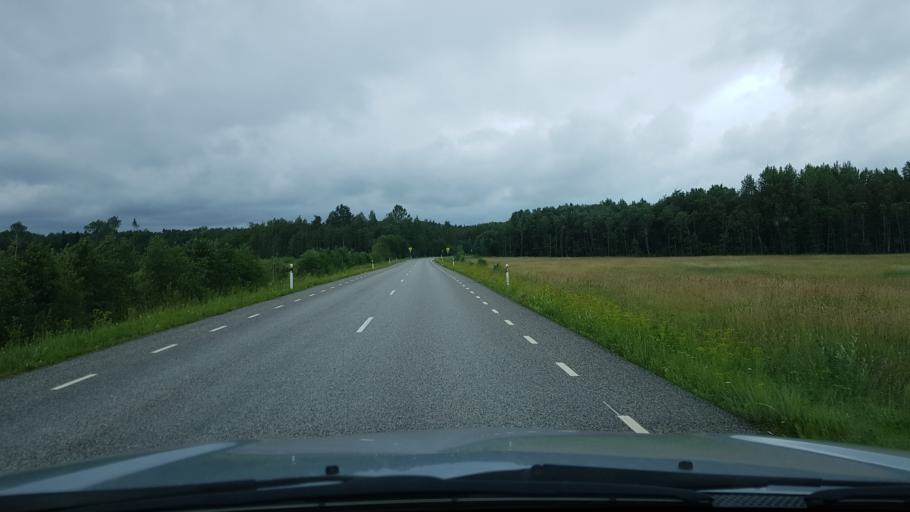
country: EE
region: Ida-Virumaa
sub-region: Narva-Joesuu linn
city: Narva-Joesuu
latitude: 59.3671
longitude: 27.9300
